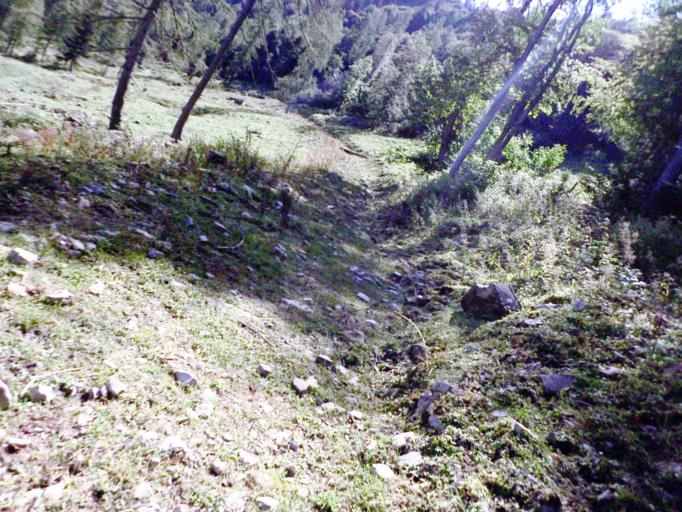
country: AT
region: Salzburg
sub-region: Politischer Bezirk Salzburg-Umgebung
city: Hintersee
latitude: 47.6930
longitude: 13.2604
